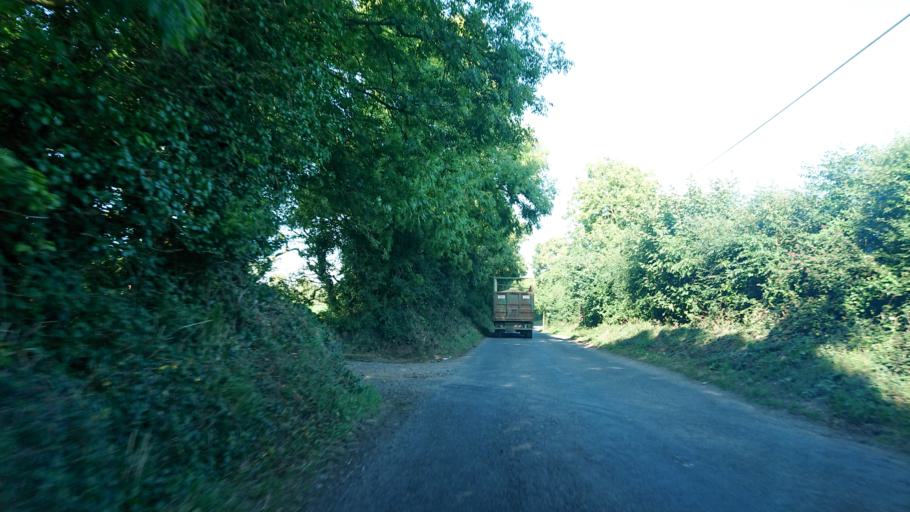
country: IE
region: Munster
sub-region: Waterford
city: Dunmore East
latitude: 52.1802
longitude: -7.0102
